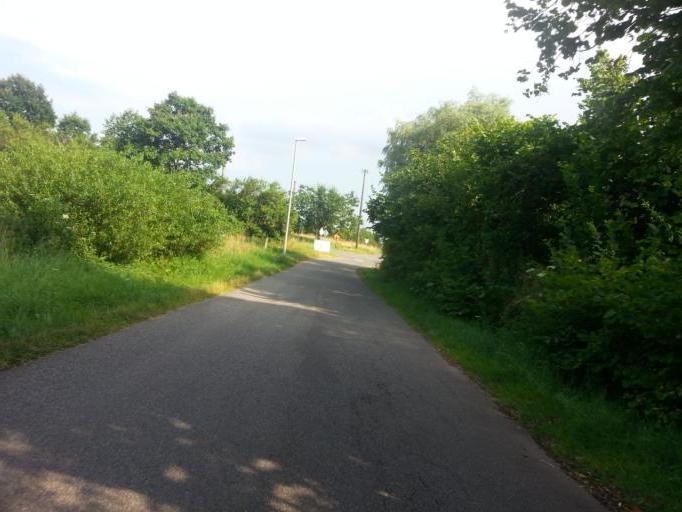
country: DE
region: Saarland
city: Oberthal
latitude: 49.5220
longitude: 7.1114
